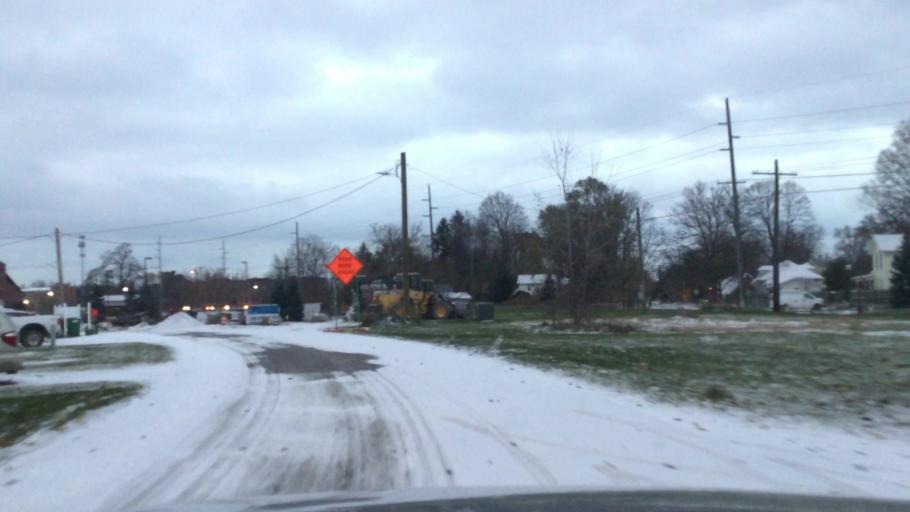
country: US
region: Michigan
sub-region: Livingston County
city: Brighton
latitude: 42.5319
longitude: -83.7876
